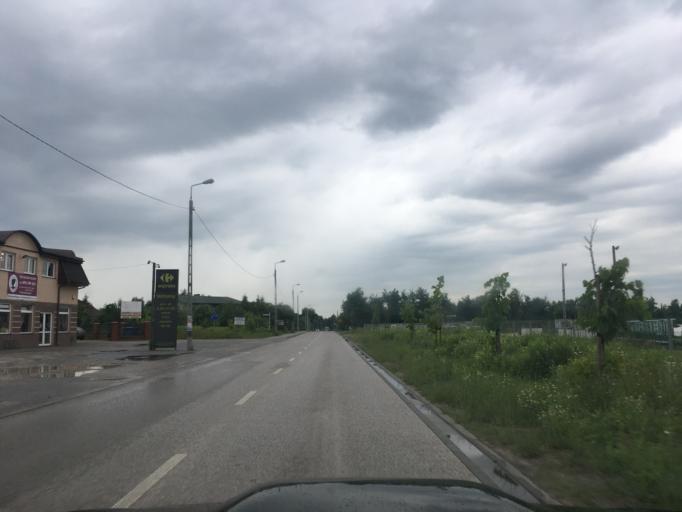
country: PL
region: Masovian Voivodeship
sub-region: Powiat piaseczynski
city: Zalesie Gorne
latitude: 52.0397
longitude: 21.0095
